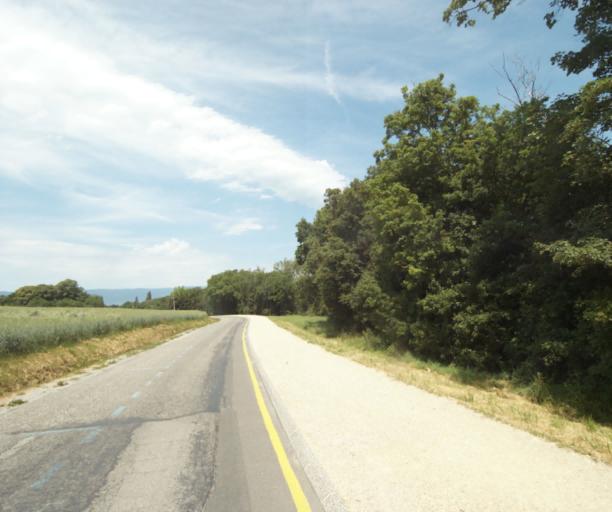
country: FR
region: Rhone-Alpes
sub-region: Departement de la Haute-Savoie
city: Chens-sur-Leman
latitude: 46.3175
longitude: 6.2659
